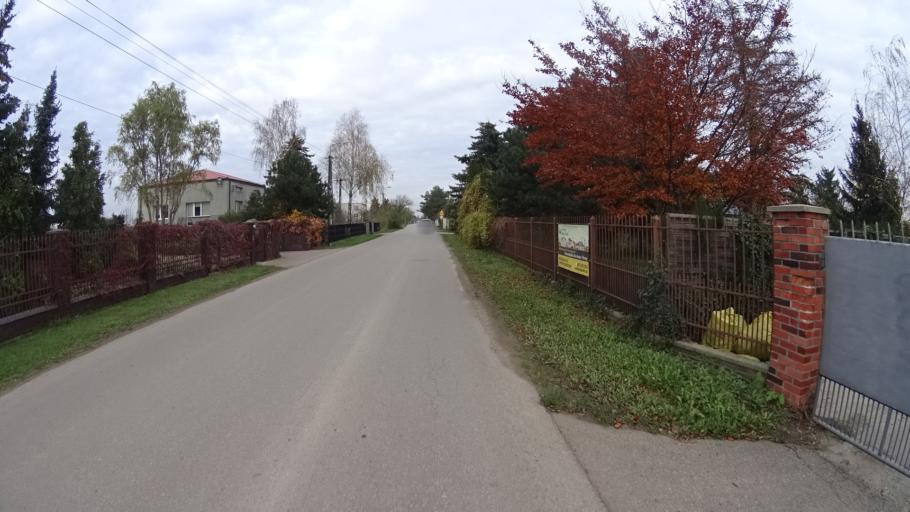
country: PL
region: Masovian Voivodeship
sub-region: Powiat warszawski zachodni
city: Stare Babice
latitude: 52.2387
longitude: 20.8284
